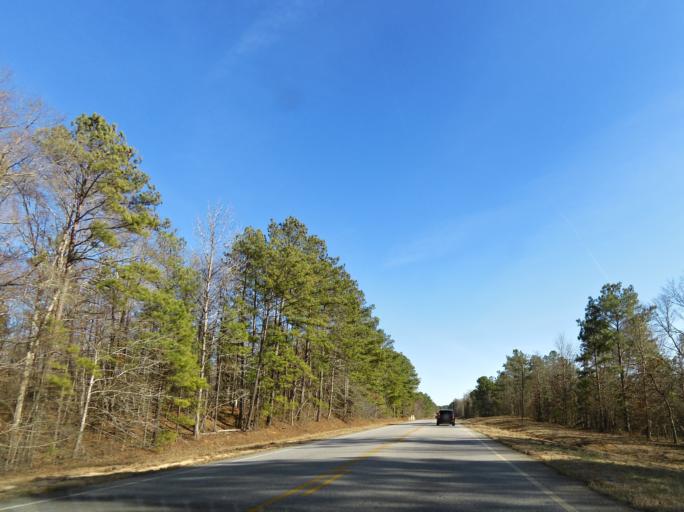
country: US
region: Georgia
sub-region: Crawford County
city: Roberta
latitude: 32.7485
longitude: -84.0783
